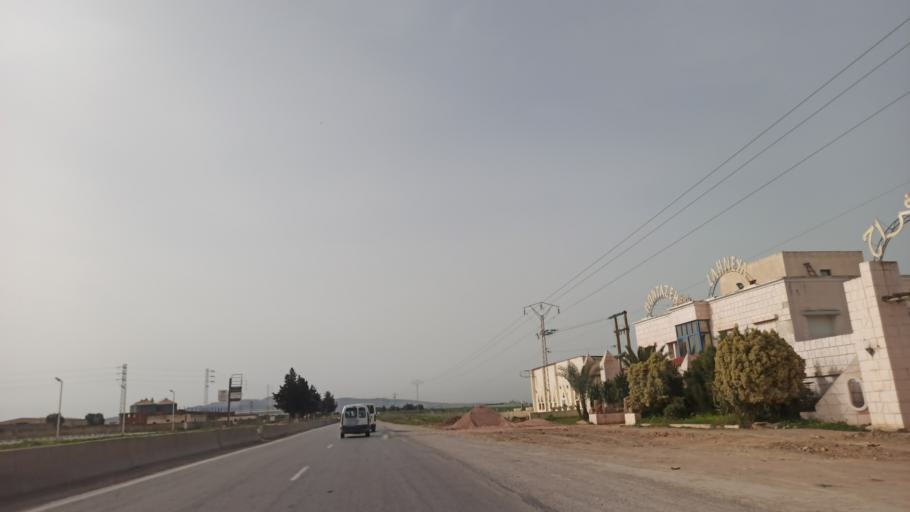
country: TN
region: Tunis
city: La Mohammedia
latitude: 36.5841
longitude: 10.0984
